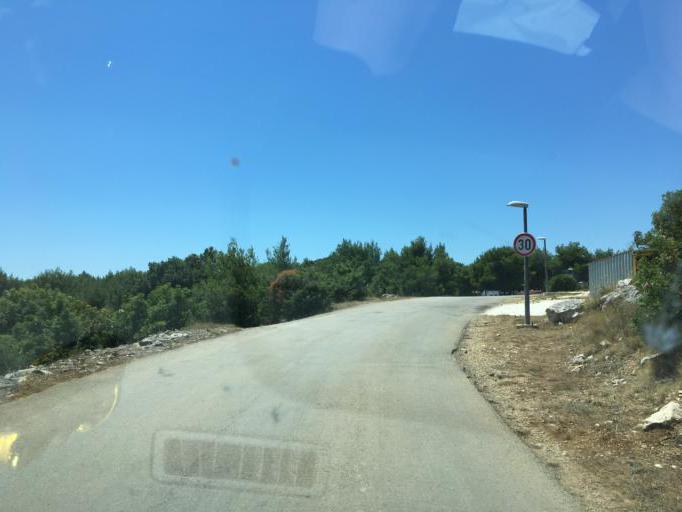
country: HR
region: Zadarska
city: Pakostane
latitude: 43.8869
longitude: 15.5346
